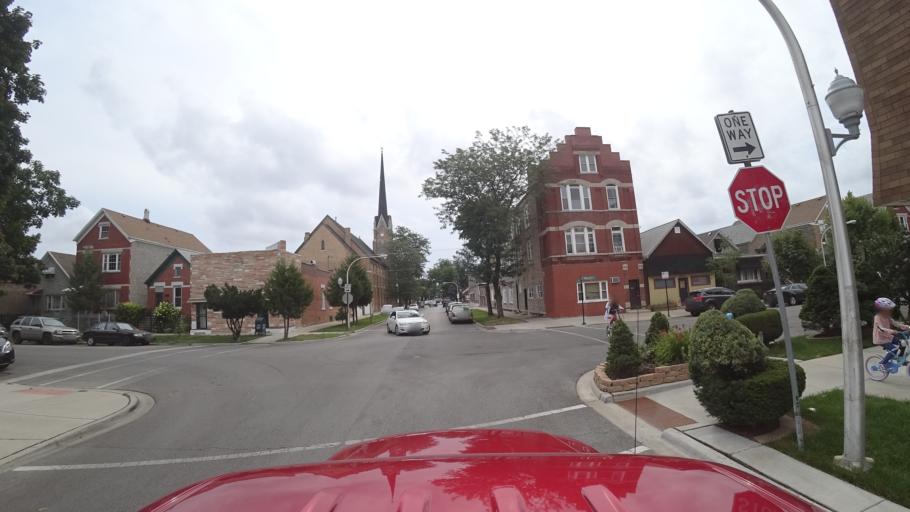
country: US
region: Illinois
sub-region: Cook County
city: Chicago
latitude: 41.8268
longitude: -87.6730
